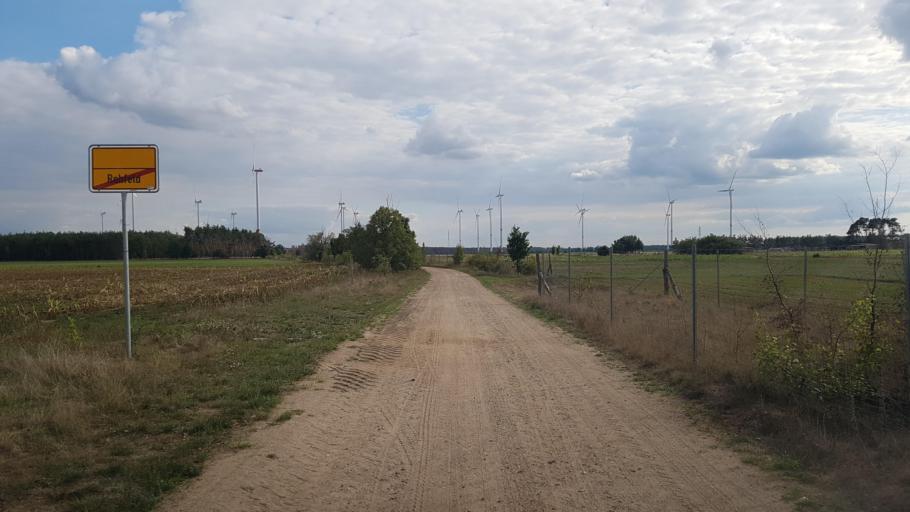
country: DE
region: Saxony
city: Arzberg
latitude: 51.5800
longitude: 13.1748
